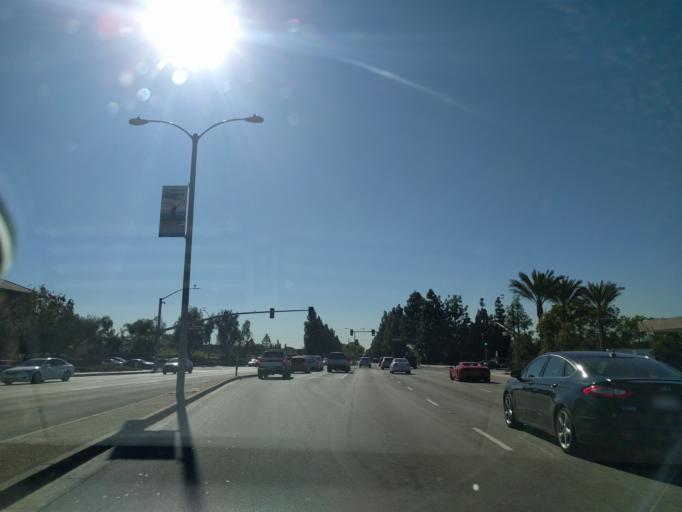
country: US
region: California
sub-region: Orange County
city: Irvine
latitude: 33.7054
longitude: -117.7871
